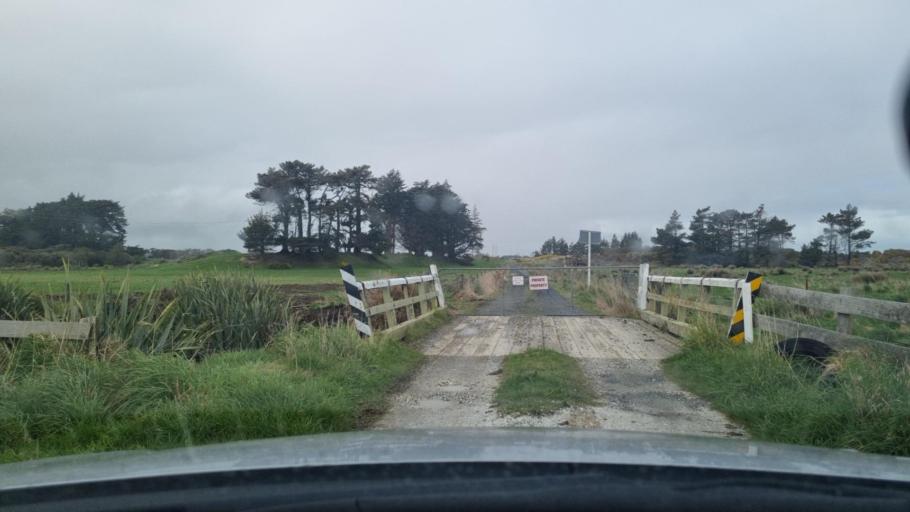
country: NZ
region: Southland
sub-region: Invercargill City
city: Bluff
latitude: -46.5118
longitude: 168.4119
